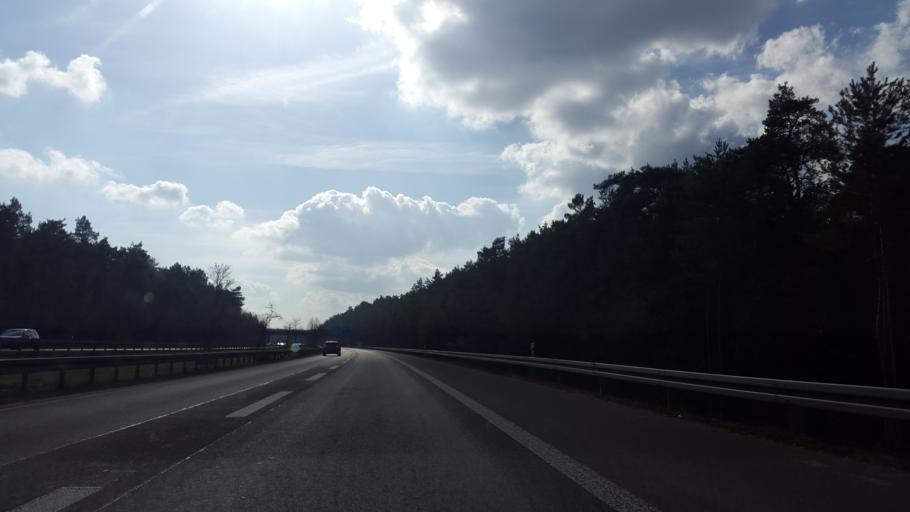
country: DE
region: Bavaria
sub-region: Regierungsbezirk Unterfranken
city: Kleinostheim
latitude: 50.0029
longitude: 9.0196
